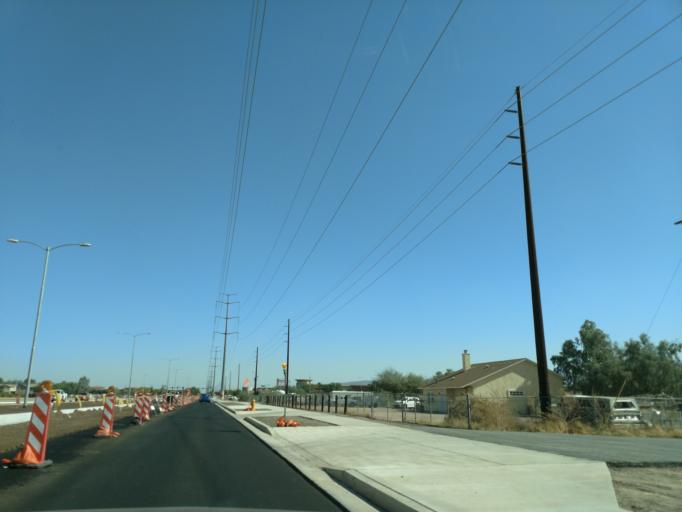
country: US
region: Arizona
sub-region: Maricopa County
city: Laveen
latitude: 33.3774
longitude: -112.1807
